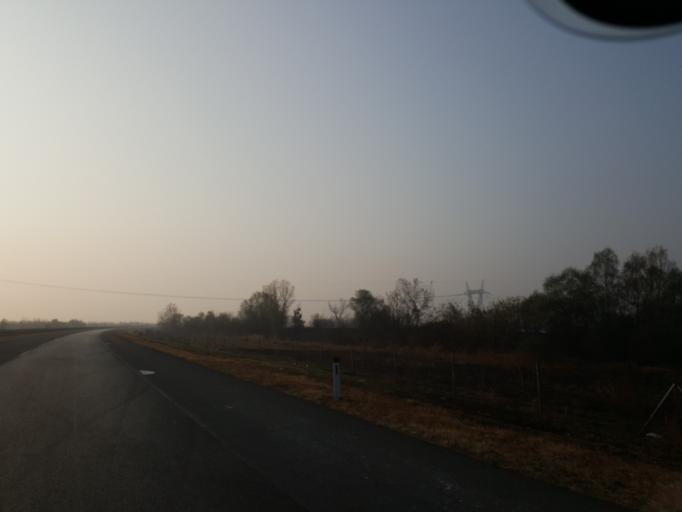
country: RS
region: Central Serbia
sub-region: Jablanicki Okrug
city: Leskovac
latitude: 43.0146
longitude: 22.0220
